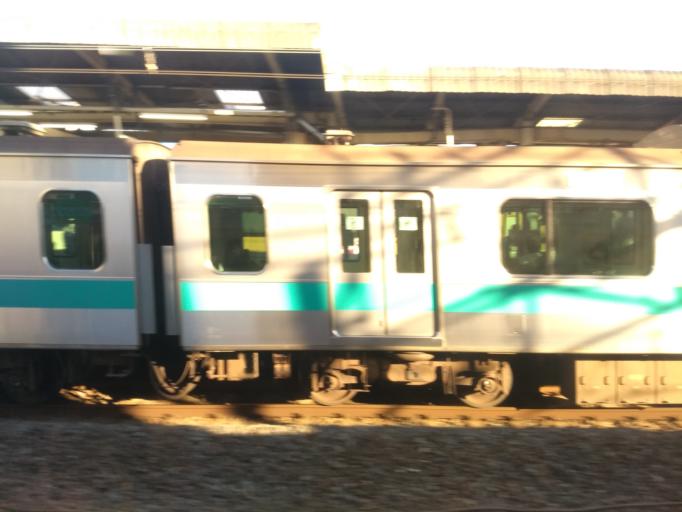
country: JP
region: Chiba
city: Nagareyama
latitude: 35.8250
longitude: 139.9210
